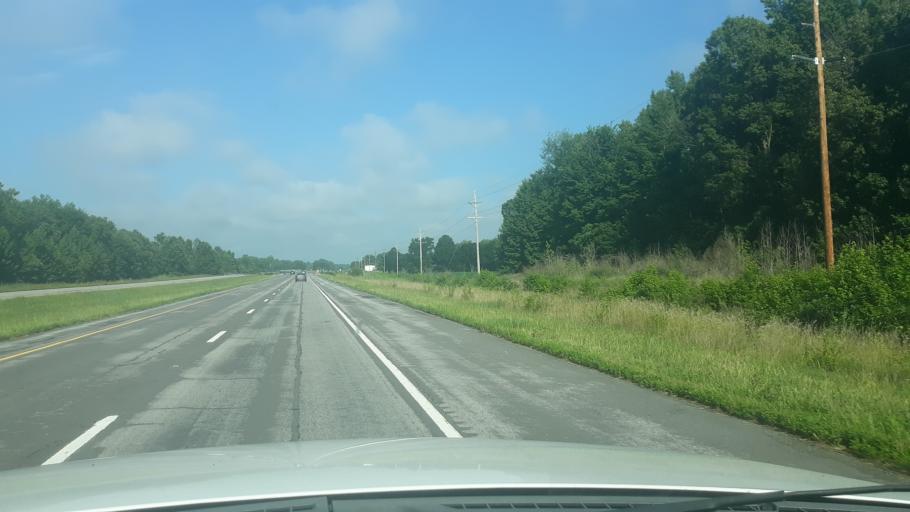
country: US
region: Illinois
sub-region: Saline County
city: Carrier Mills
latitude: 37.7336
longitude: -88.6646
